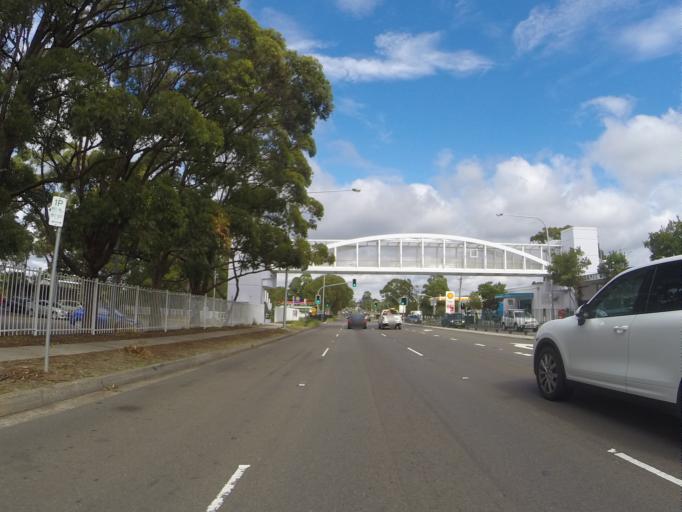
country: AU
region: New South Wales
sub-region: Sutherland Shire
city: Heathcote
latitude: -34.0870
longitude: 151.0086
